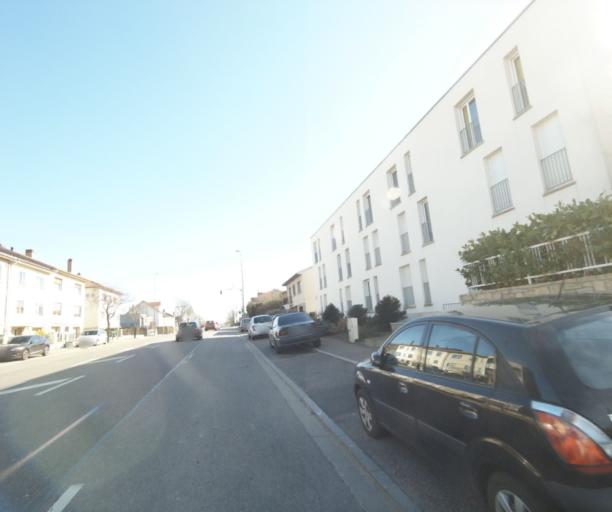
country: FR
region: Lorraine
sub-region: Departement de Meurthe-et-Moselle
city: Villers-les-Nancy
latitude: 48.6750
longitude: 6.1502
